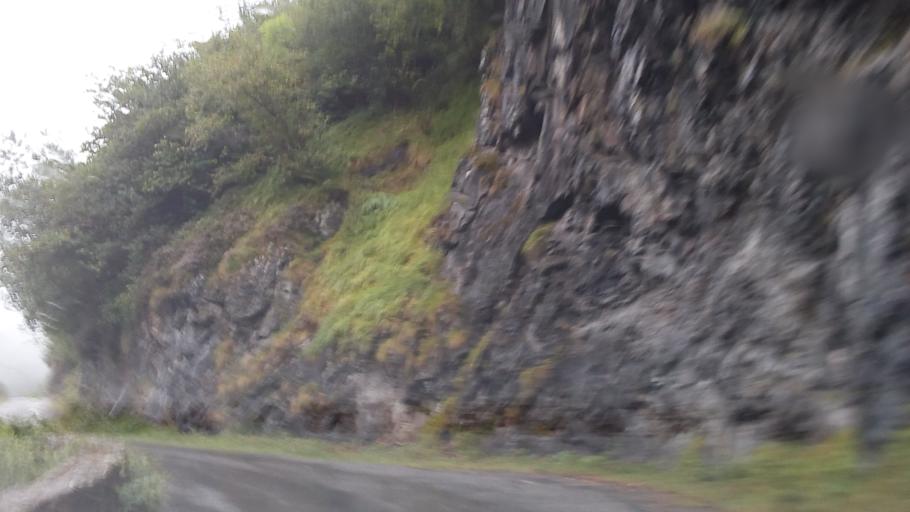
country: FR
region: Midi-Pyrenees
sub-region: Departement des Hautes-Pyrenees
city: Cauterets
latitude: 42.9182
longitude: -0.2544
